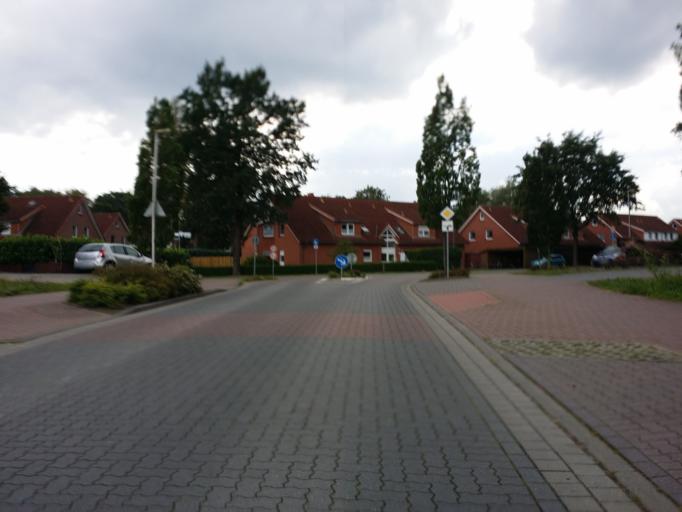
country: DE
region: Lower Saxony
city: Hemmoor
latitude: 53.6838
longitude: 9.1657
